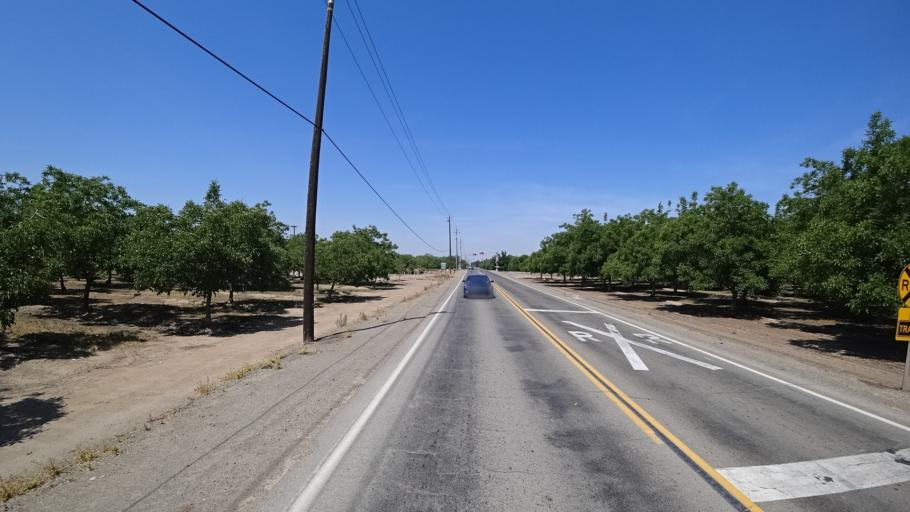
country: US
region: California
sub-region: Kings County
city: Lucerne
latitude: 36.4011
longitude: -119.6626
